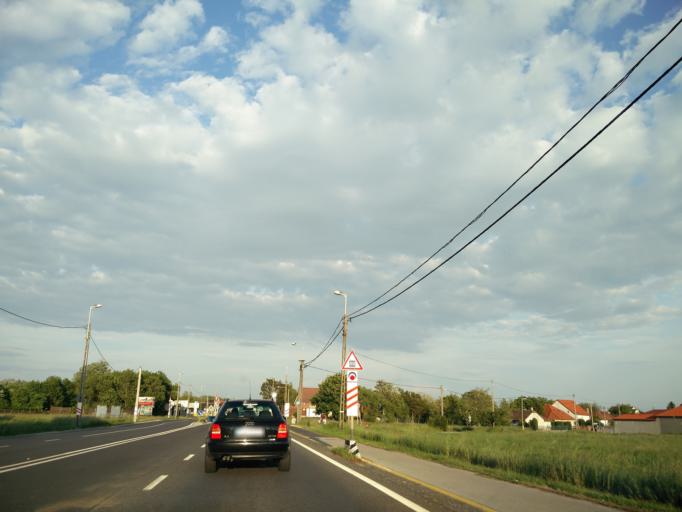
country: HU
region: Fejer
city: Szekesfehervar
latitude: 47.2086
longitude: 18.3733
